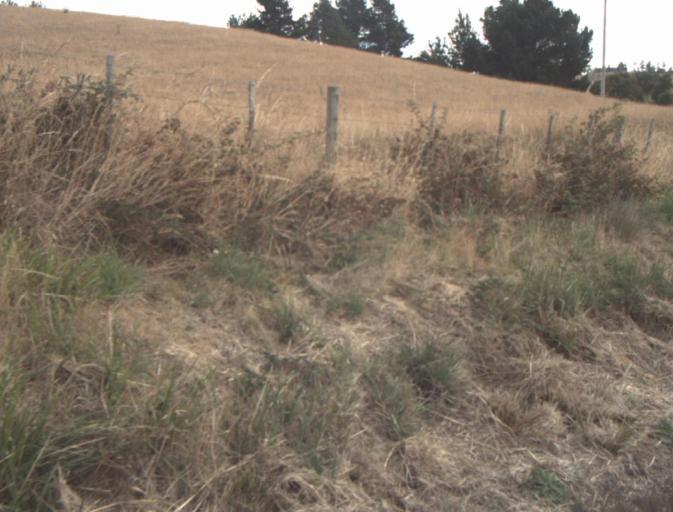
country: AU
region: Tasmania
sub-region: Launceston
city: Mayfield
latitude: -41.2105
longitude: 147.1093
